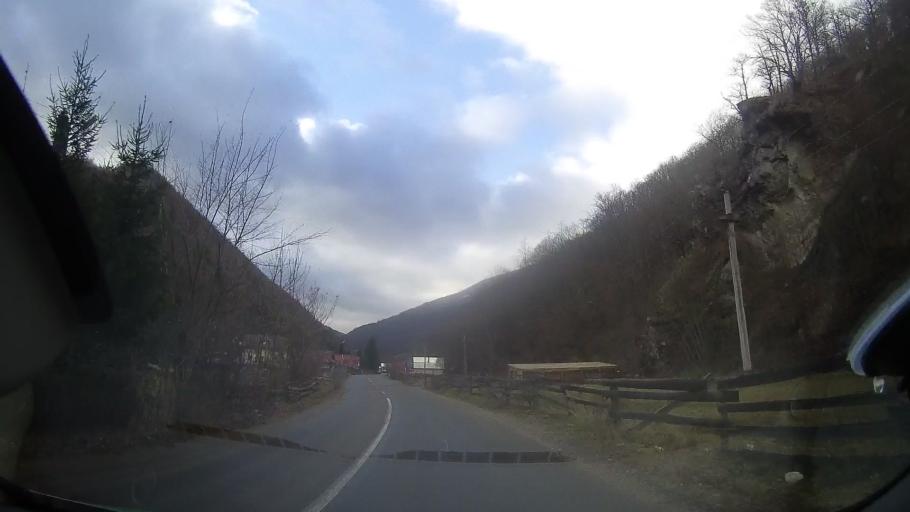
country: RO
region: Cluj
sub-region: Comuna Valea Ierii
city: Valea Ierii
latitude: 46.6862
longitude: 23.2755
